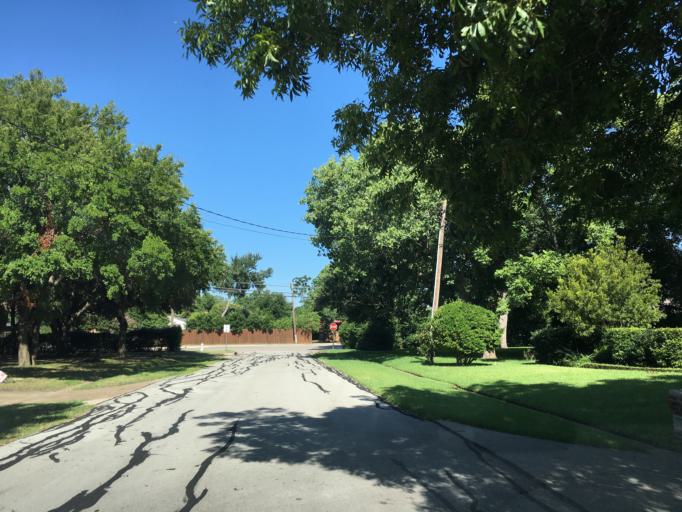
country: US
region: Texas
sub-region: Dallas County
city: Farmers Branch
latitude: 32.9230
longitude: -96.8723
